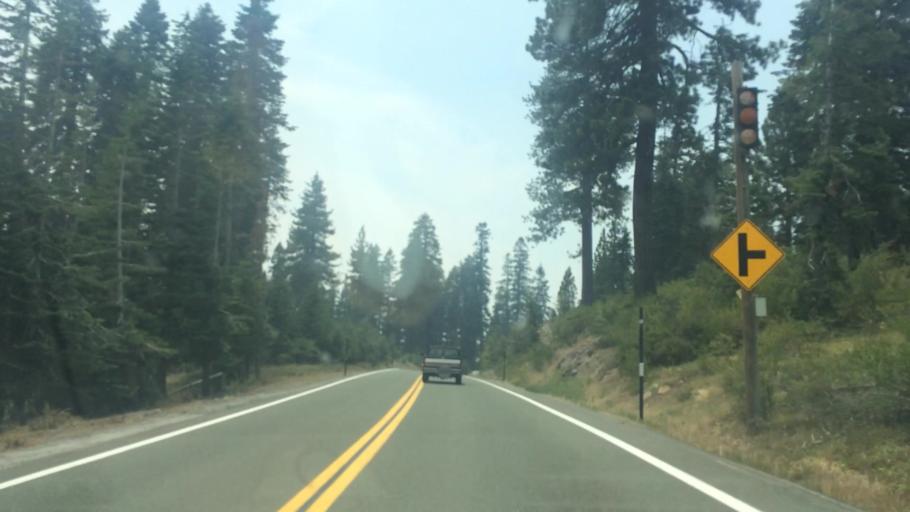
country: US
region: California
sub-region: Calaveras County
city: Arnold
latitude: 38.5833
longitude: -120.2516
